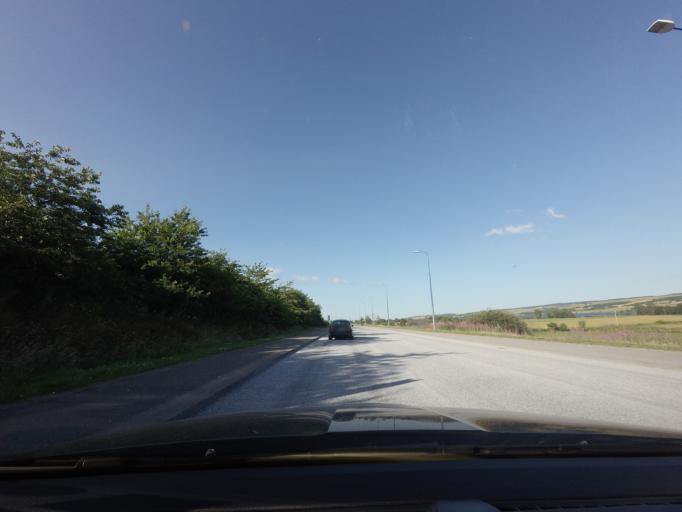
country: GB
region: Scotland
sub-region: Highland
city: Dingwall
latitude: 57.5853
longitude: -4.4296
